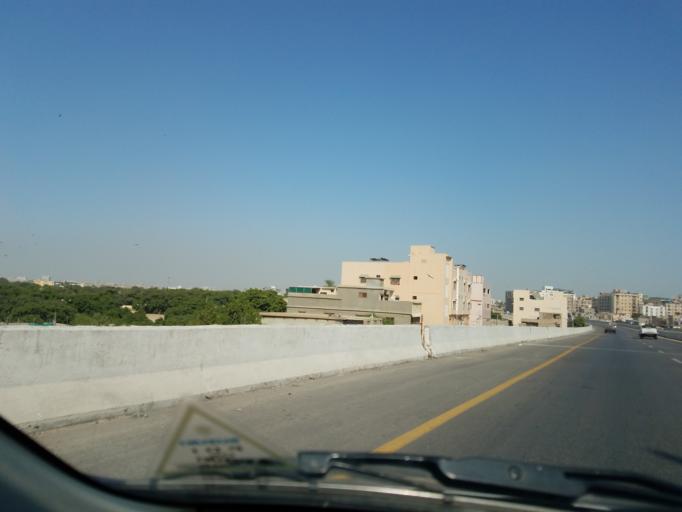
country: PK
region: Sindh
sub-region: Karachi District
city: Karachi
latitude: 24.8792
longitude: 67.0111
